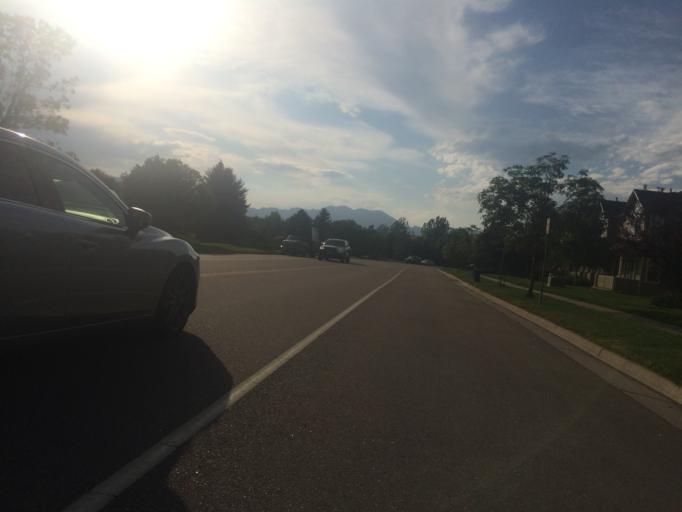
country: US
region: Colorado
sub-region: Boulder County
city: Superior
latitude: 39.9271
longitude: -105.1513
